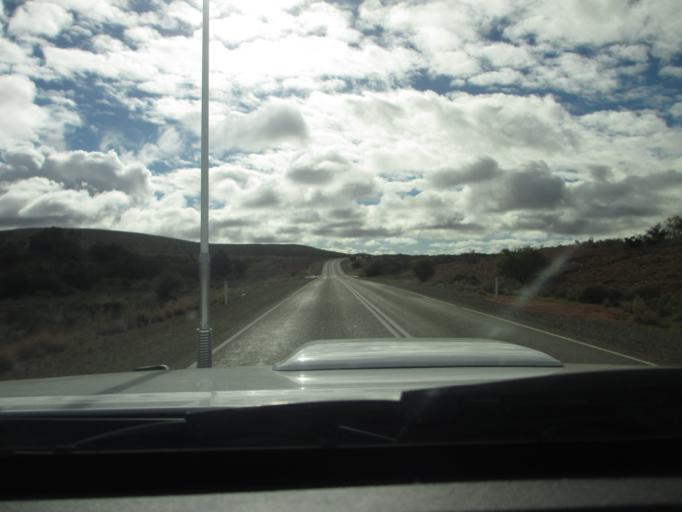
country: AU
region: South Australia
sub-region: Flinders Ranges
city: Quorn
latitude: -32.2101
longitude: 138.5221
